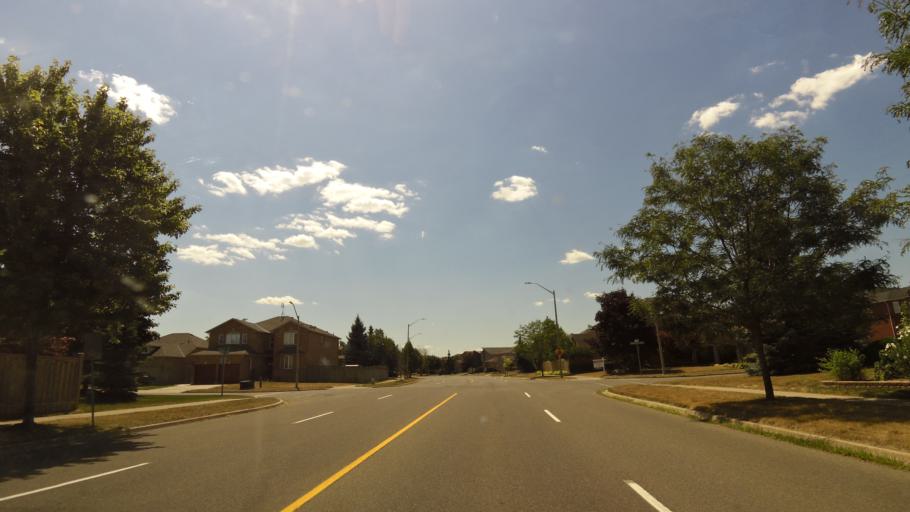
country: CA
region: Ontario
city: Brampton
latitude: 43.6390
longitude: -79.8745
